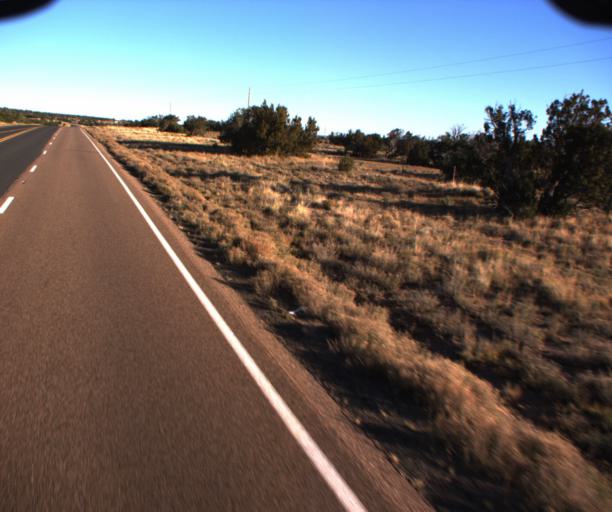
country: US
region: Arizona
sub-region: Apache County
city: Ganado
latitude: 35.4187
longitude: -109.5140
